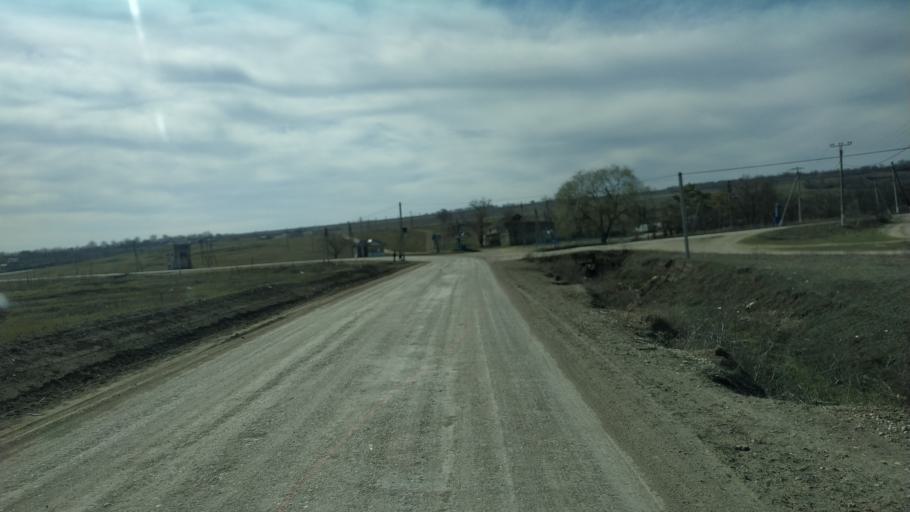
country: MD
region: Nisporeni
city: Nisporeni
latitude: 46.9702
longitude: 28.1824
